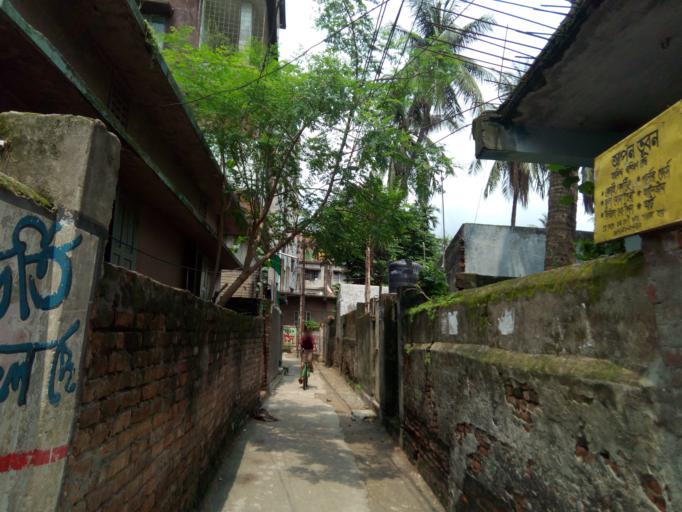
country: BD
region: Dhaka
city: Azimpur
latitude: 23.7445
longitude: 90.3645
